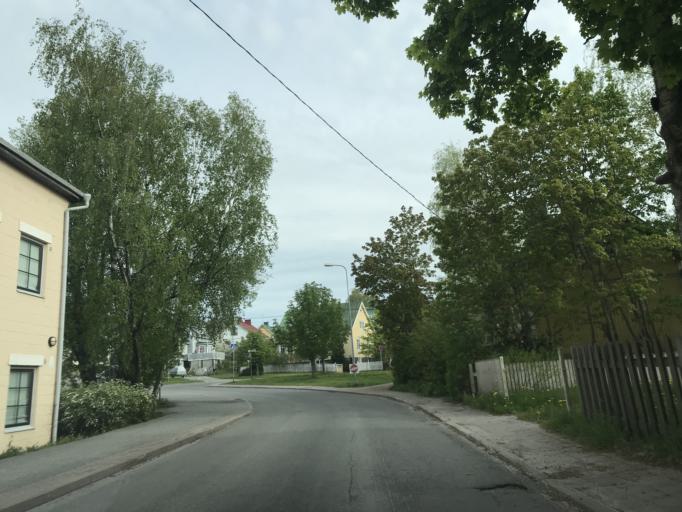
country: FI
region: Varsinais-Suomi
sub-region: Turku
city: Turku
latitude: 60.4547
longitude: 22.3064
